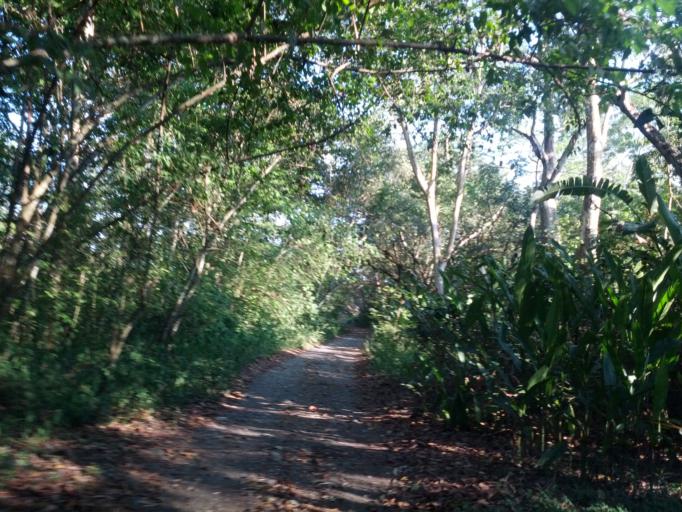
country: CR
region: Puntarenas
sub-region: Canton de Golfito
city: Golfito
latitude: 8.5085
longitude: -83.2931
